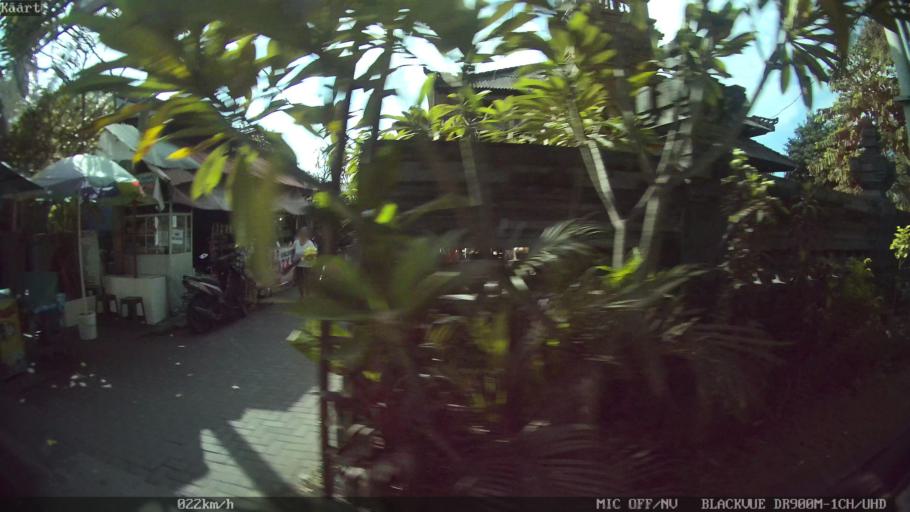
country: ID
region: Bali
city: Karyadharma
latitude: -8.6878
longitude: 115.1969
